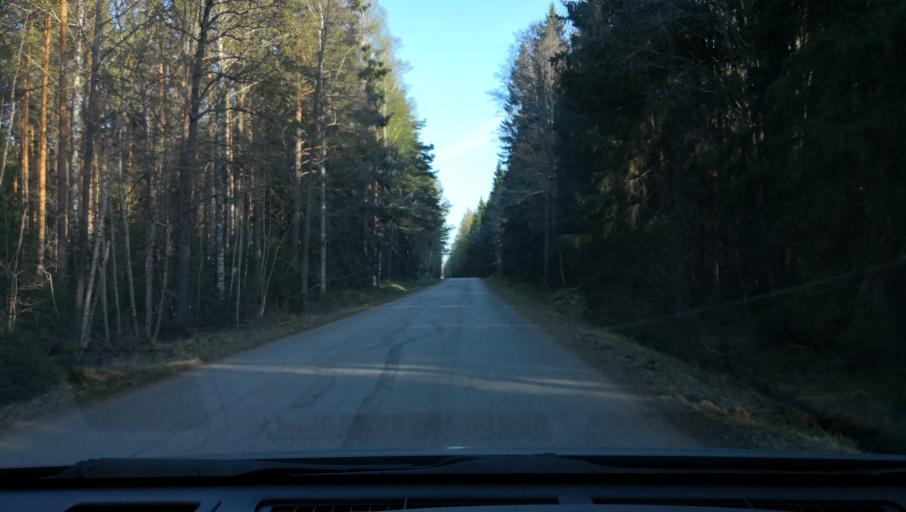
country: SE
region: Uppsala
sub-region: Heby Kommun
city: Tarnsjo
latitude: 60.2792
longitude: 16.8906
